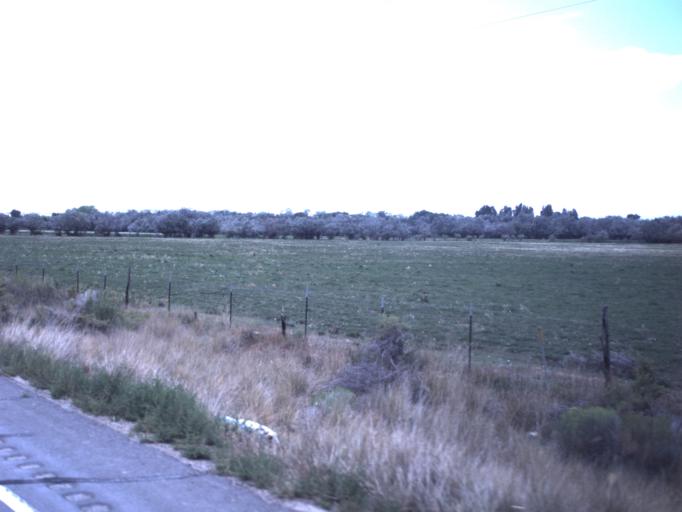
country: US
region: Utah
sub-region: Duchesne County
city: Roosevelt
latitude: 40.1706
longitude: -110.1402
